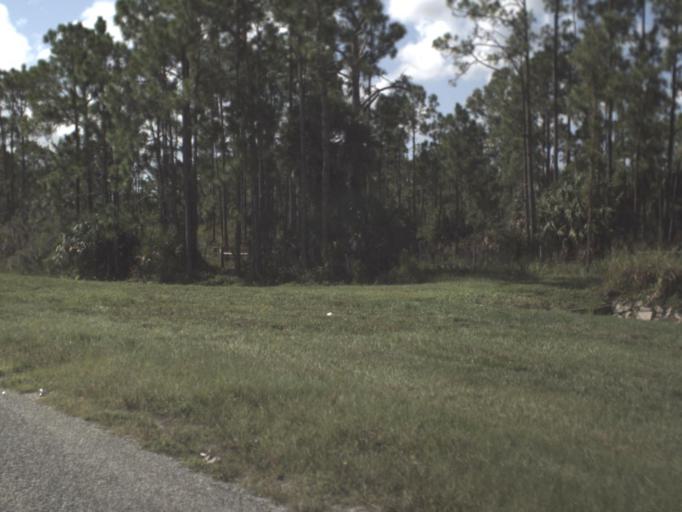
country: US
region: Florida
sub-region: Lee County
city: Burnt Store Marina
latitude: 26.8220
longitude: -81.9648
